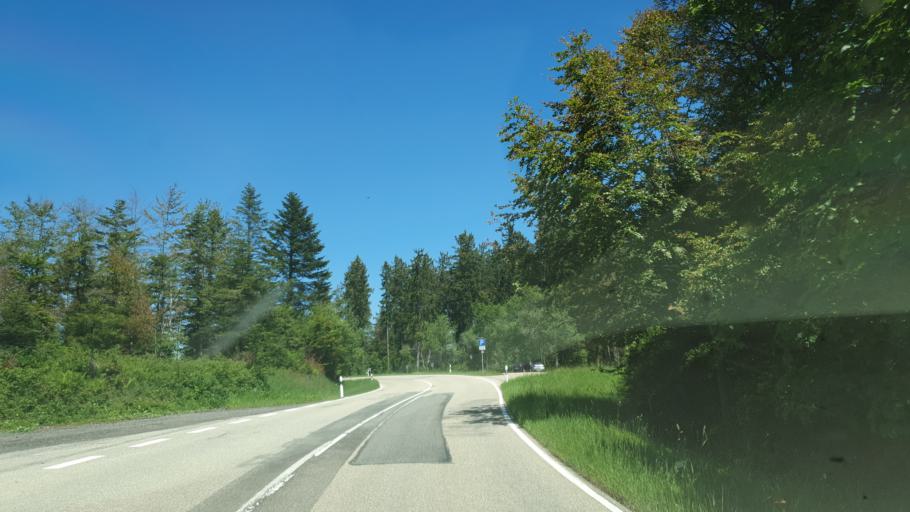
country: DE
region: Baden-Wuerttemberg
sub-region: Freiburg Region
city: Wieden
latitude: 47.8847
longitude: 7.8962
